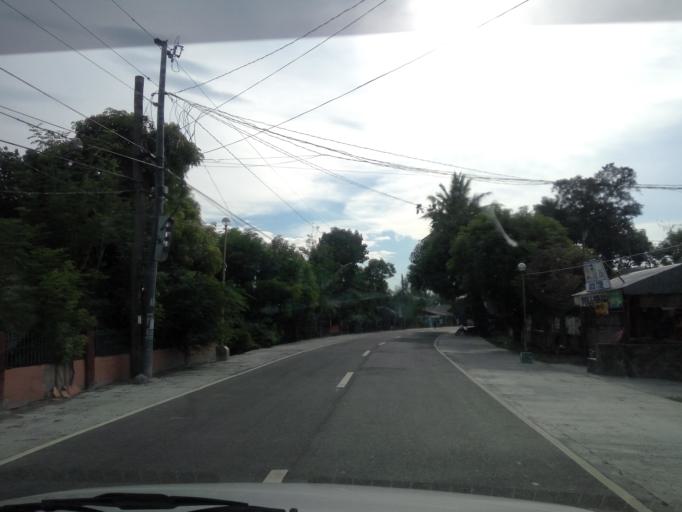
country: PH
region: Ilocos
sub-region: Province of Pangasinan
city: Calepaan
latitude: 16.0302
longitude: 120.6242
